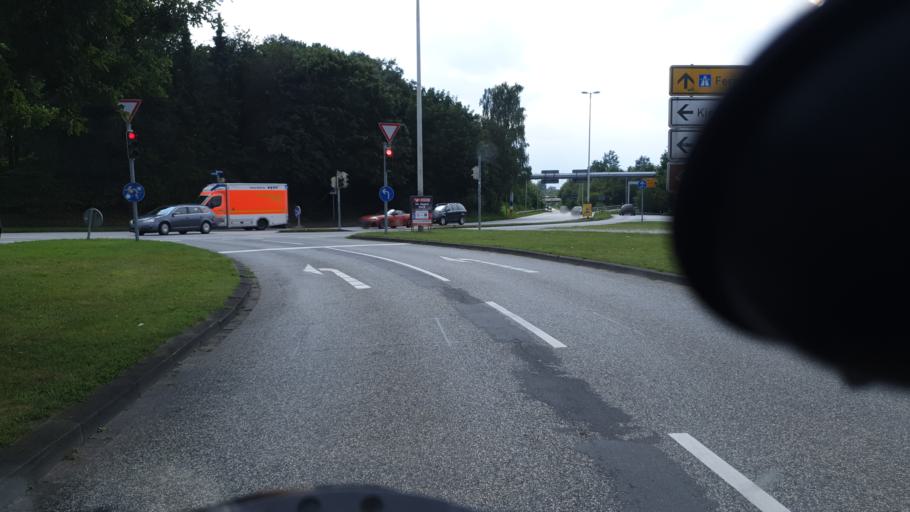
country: DE
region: Schleswig-Holstein
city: Kiel
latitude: 54.3484
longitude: 10.1253
